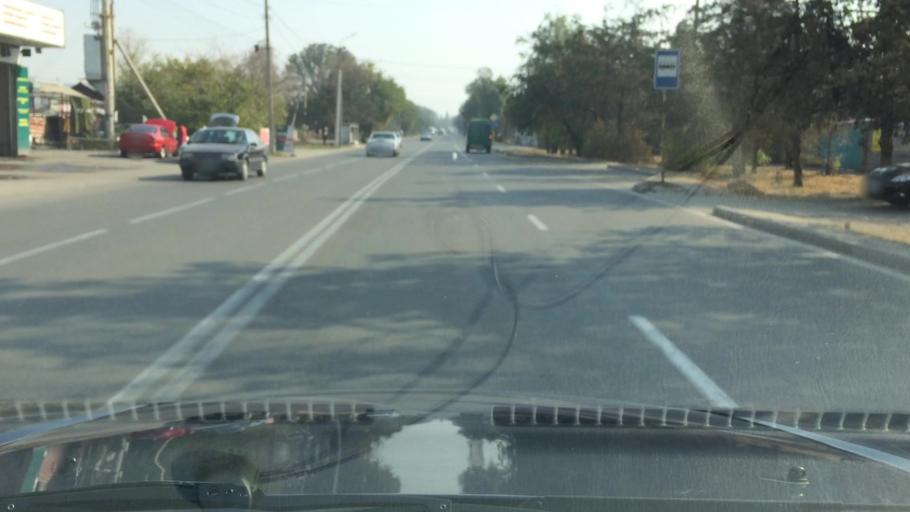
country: KG
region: Chuy
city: Lebedinovka
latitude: 42.8840
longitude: 74.6481
